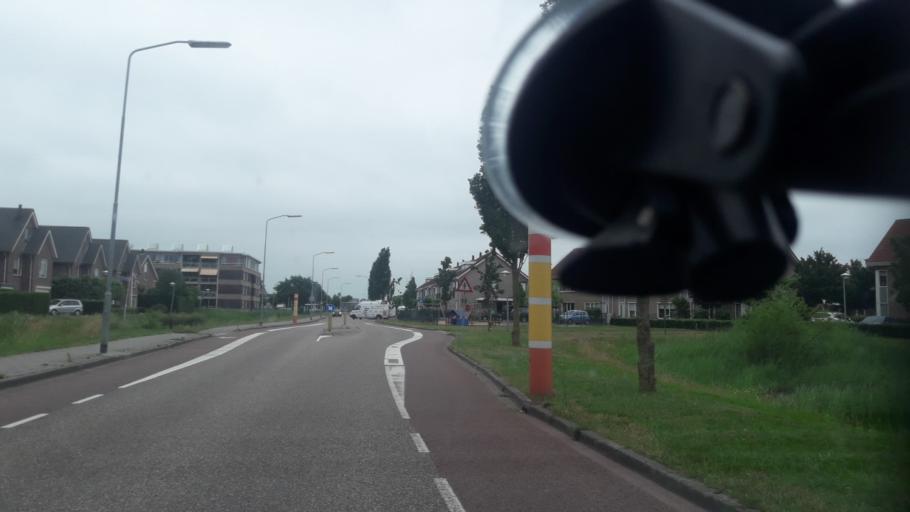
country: NL
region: Gelderland
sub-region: Gemeente Elburg
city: Elburg
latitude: 52.4468
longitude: 5.8608
